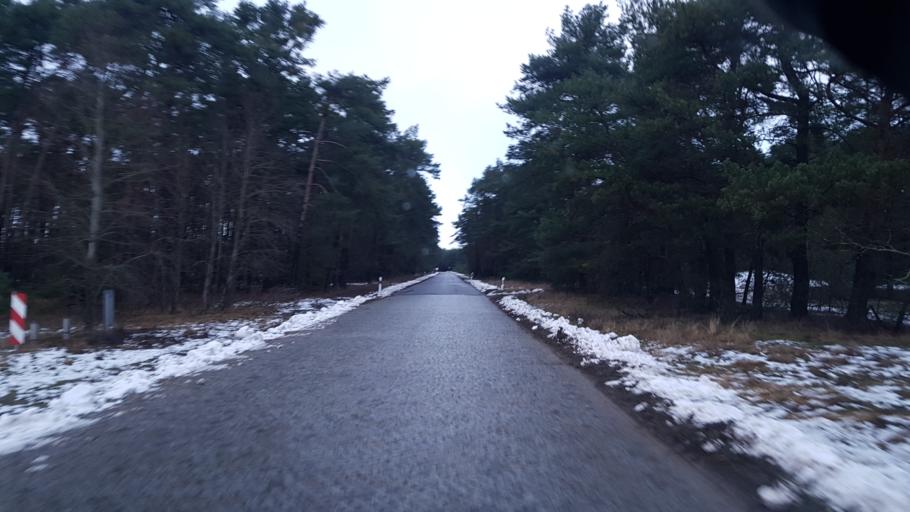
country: DE
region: Brandenburg
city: Janschwalde
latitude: 51.8717
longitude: 14.5089
